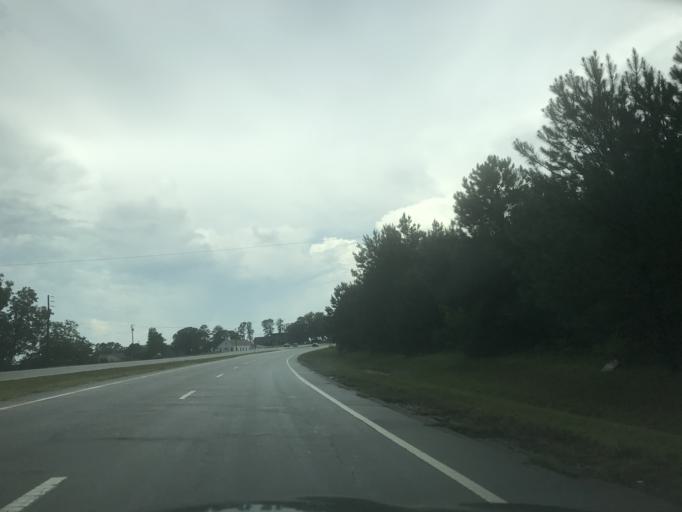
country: US
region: North Carolina
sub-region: Johnston County
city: Wilsons Mills
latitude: 35.5562
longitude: -78.3876
